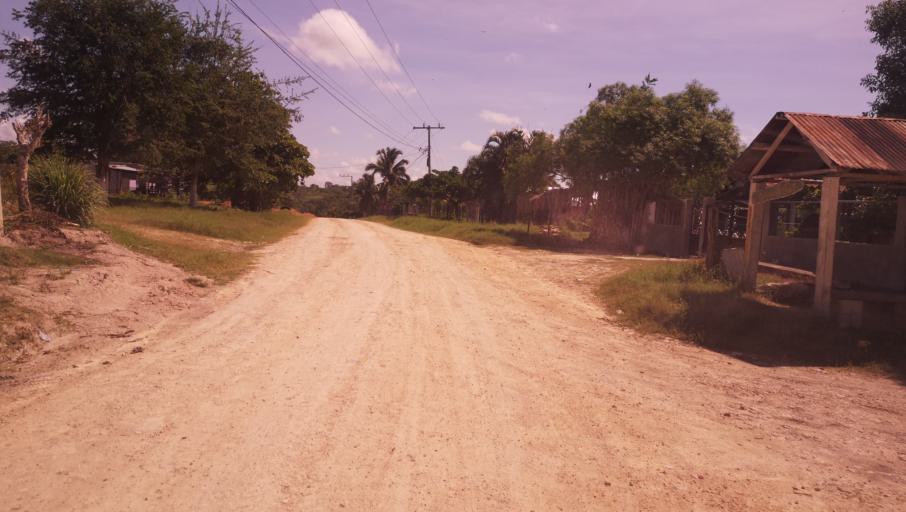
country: GT
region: Peten
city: Melchor de Mencos
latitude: 16.9317
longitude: -89.2765
